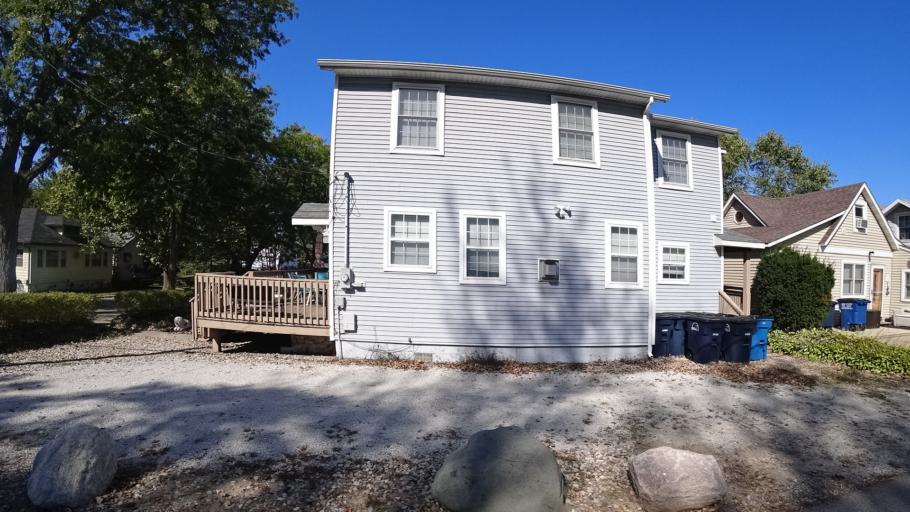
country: US
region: Indiana
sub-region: LaPorte County
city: Michigan City
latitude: 41.7289
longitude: -86.8924
